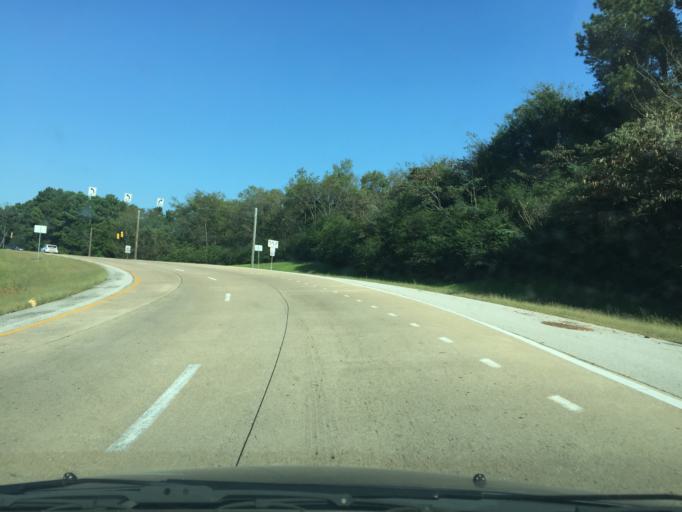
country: US
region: Tennessee
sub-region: Hamilton County
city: East Chattanooga
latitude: 35.0906
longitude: -85.2168
